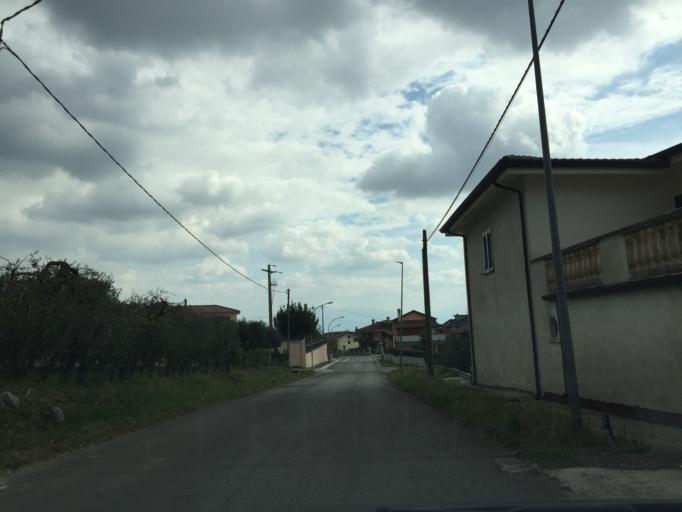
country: IT
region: Latium
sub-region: Provincia di Frosinone
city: Piedimonte San Germano
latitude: 41.4998
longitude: 13.7423
